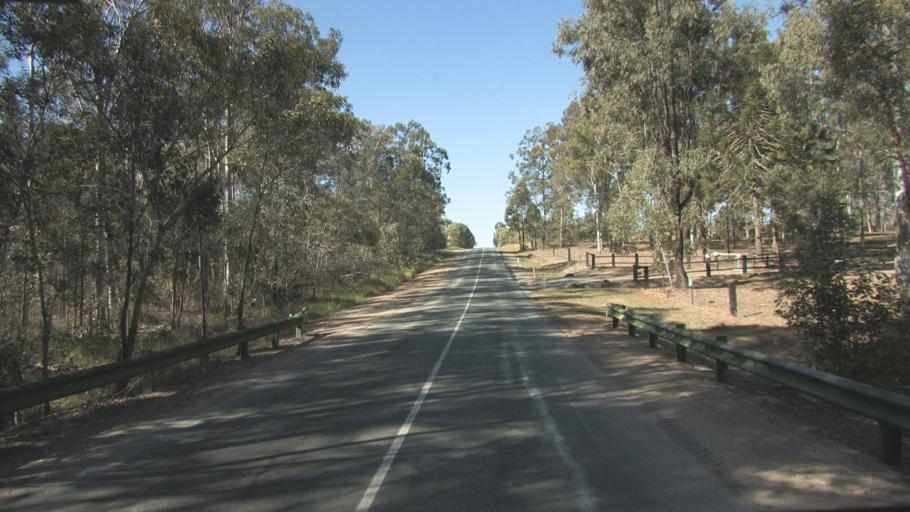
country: AU
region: Queensland
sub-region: Ipswich
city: Springfield Lakes
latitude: -27.7308
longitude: 152.9329
